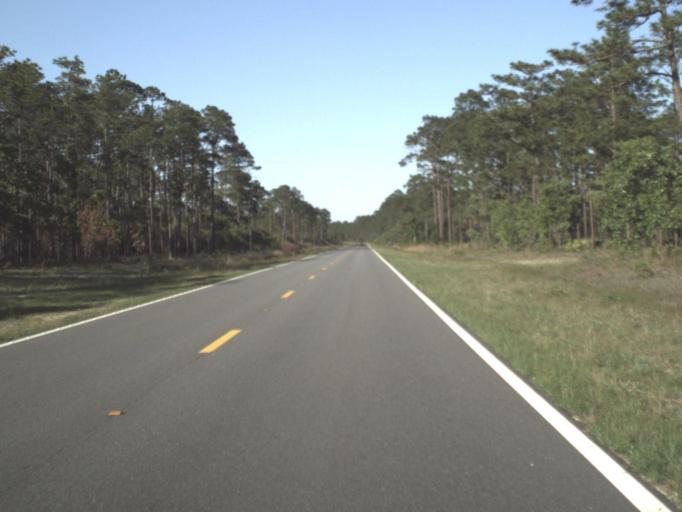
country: US
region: Florida
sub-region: Liberty County
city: Bristol
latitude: 30.2044
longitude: -84.9074
